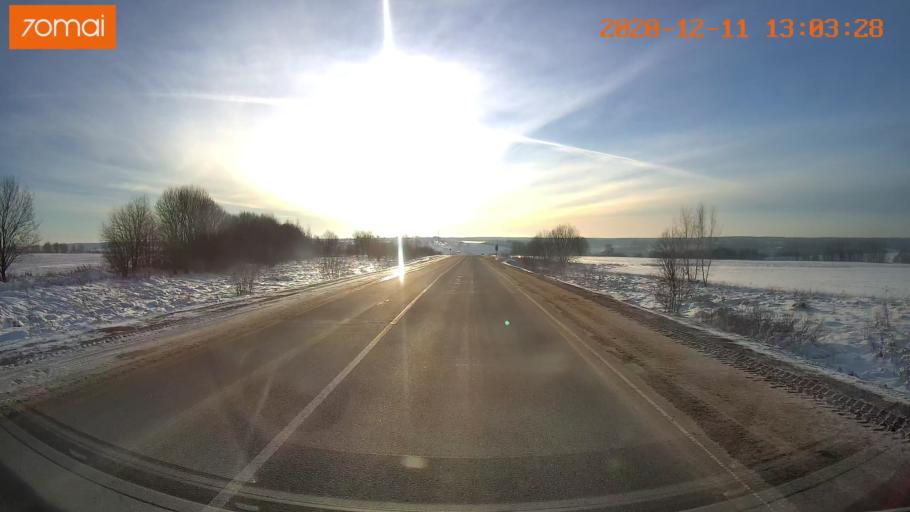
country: RU
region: Kostroma
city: Chistyye Bory
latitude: 58.2694
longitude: 41.6749
